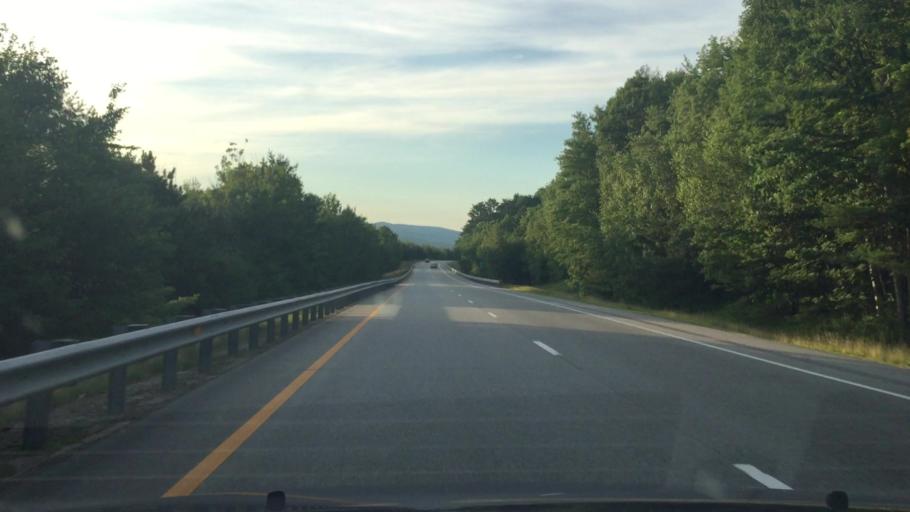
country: US
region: New Hampshire
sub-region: Grafton County
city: Ashland
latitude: 43.7202
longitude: -71.6539
